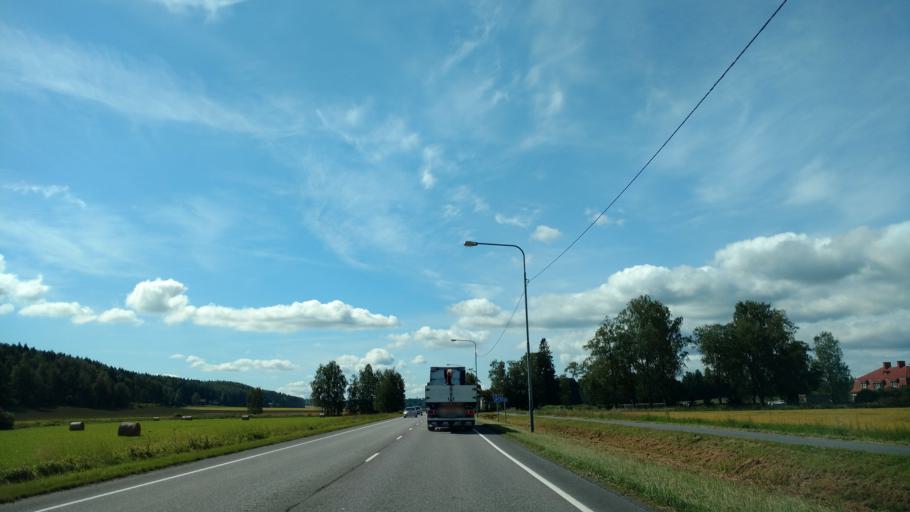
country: FI
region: Varsinais-Suomi
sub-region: Salo
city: Pernioe
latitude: 60.2442
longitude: 23.1296
